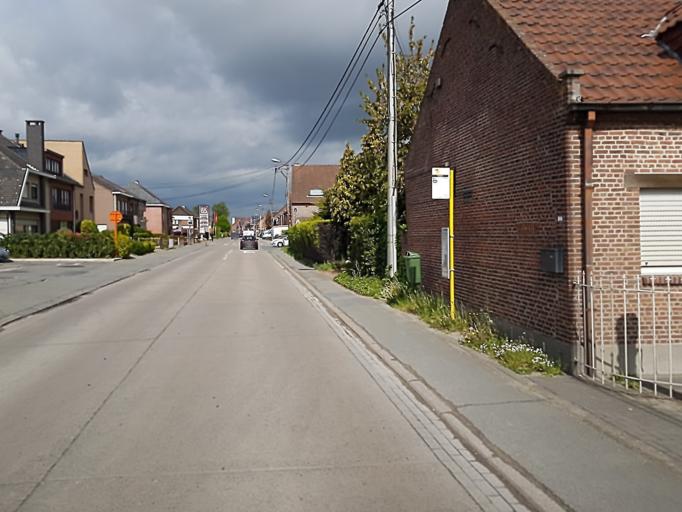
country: BE
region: Flanders
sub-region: Provincie Vlaams-Brabant
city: Londerzeel
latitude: 51.0004
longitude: 4.3110
